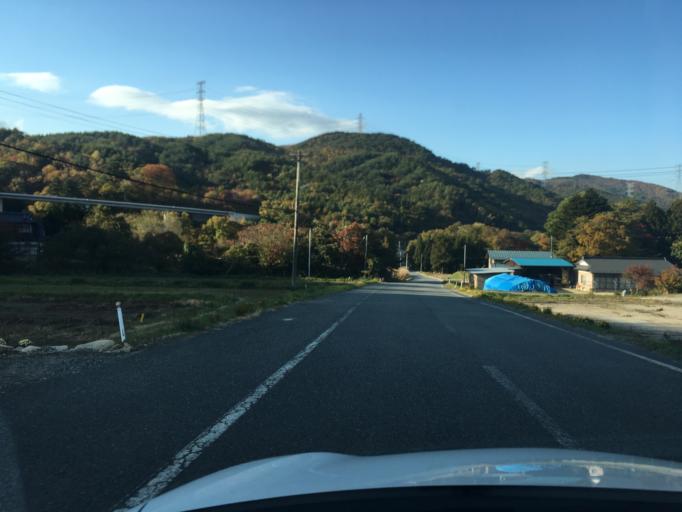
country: JP
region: Fukushima
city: Funehikimachi-funehiki
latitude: 37.2886
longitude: 140.7598
